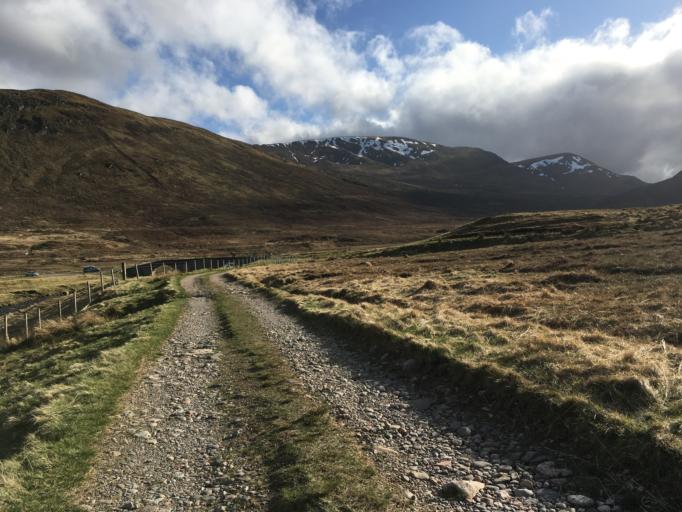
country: GB
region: Scotland
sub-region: Highland
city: Kingussie
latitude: 57.0219
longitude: -4.4355
